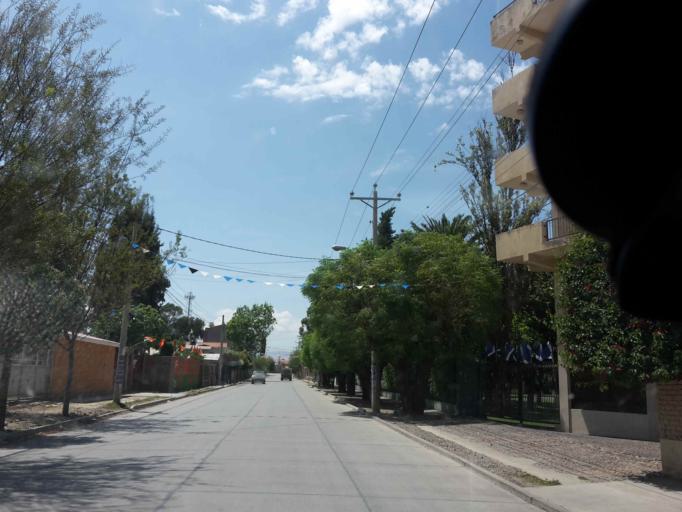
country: BO
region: Cochabamba
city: Cochabamba
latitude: -17.3691
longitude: -66.2092
